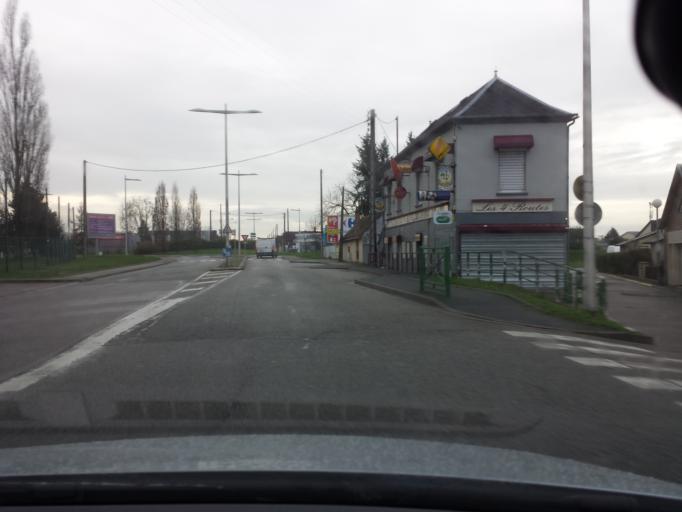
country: FR
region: Haute-Normandie
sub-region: Departement de l'Eure
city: Evreux
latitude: 49.0044
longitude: 1.1513
